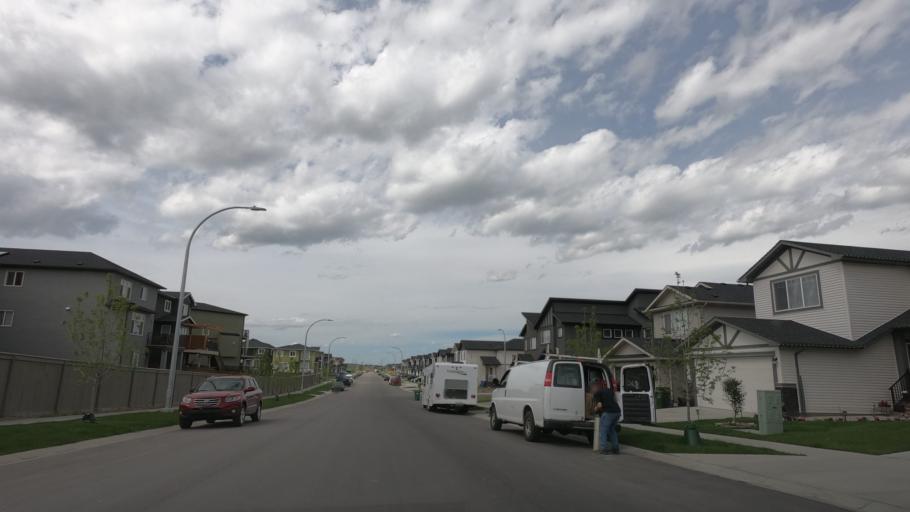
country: CA
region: Alberta
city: Airdrie
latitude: 51.2755
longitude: -114.0438
